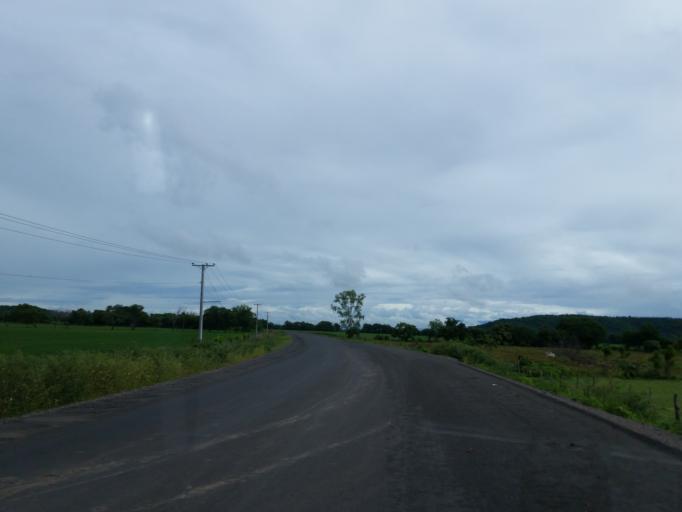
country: NI
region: Leon
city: Larreynaga
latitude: 12.5063
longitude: -86.6040
